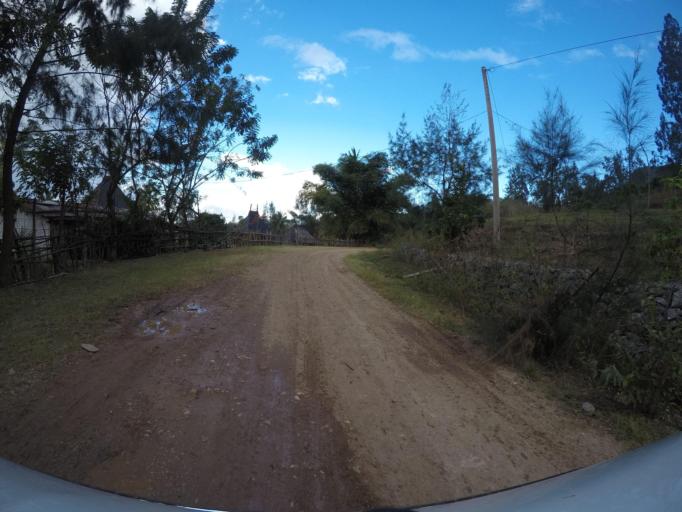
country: TL
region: Baucau
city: Venilale
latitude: -8.6871
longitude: 126.6603
